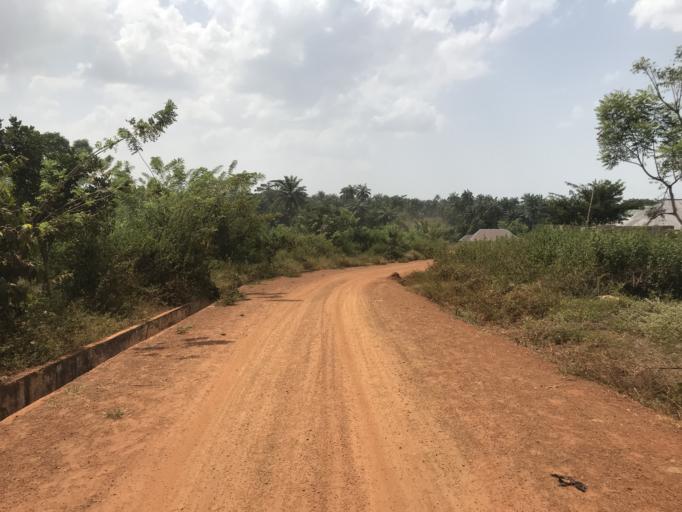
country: NG
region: Osun
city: Ikirun
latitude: 7.9353
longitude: 4.6384
